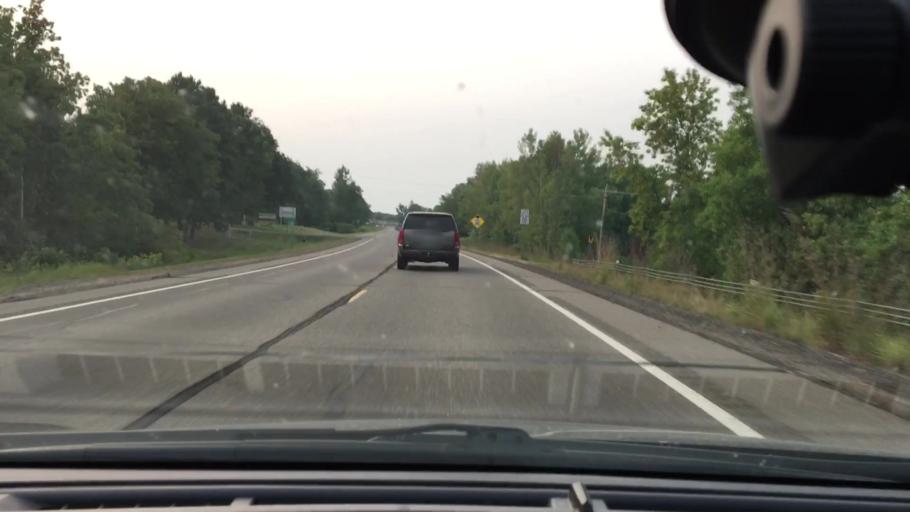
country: US
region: Minnesota
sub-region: Crow Wing County
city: Crosby
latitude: 46.4689
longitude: -93.8877
